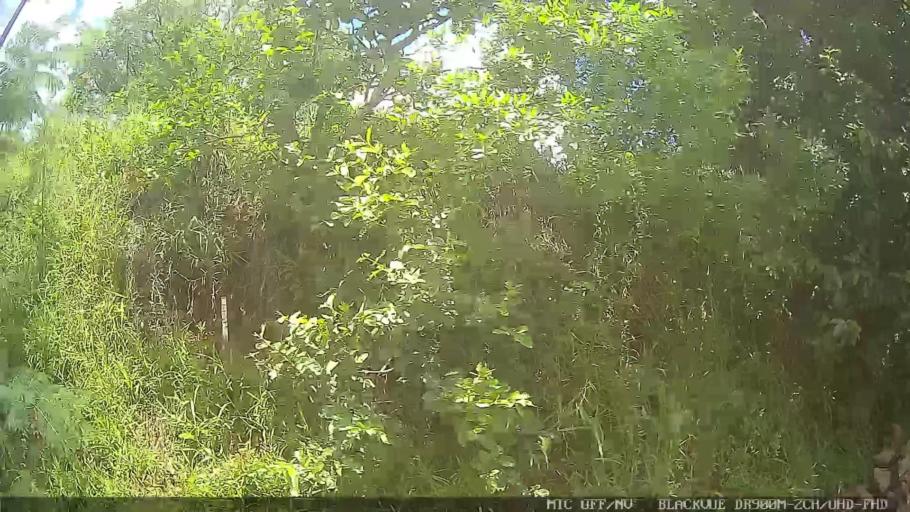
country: BR
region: Minas Gerais
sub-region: Extrema
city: Extrema
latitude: -22.8691
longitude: -46.3263
